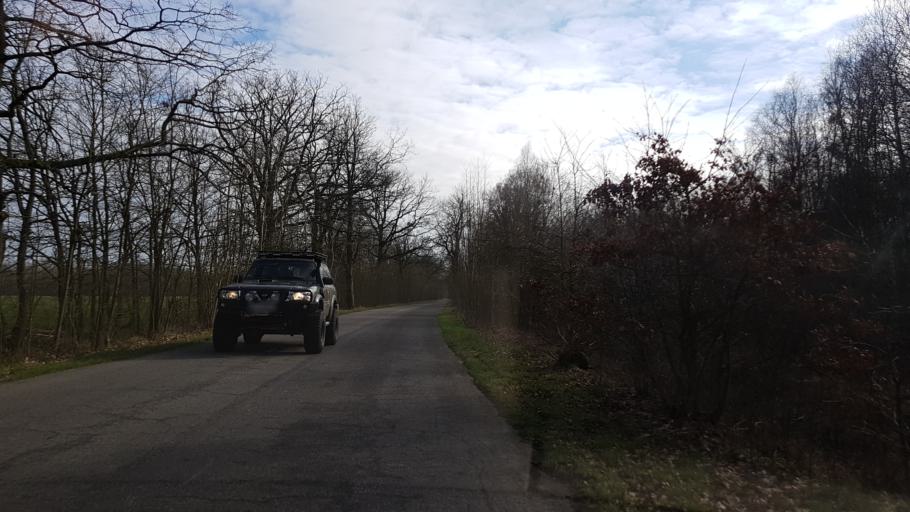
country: PL
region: West Pomeranian Voivodeship
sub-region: Powiat policki
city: Dobra
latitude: 53.5350
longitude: 14.3220
